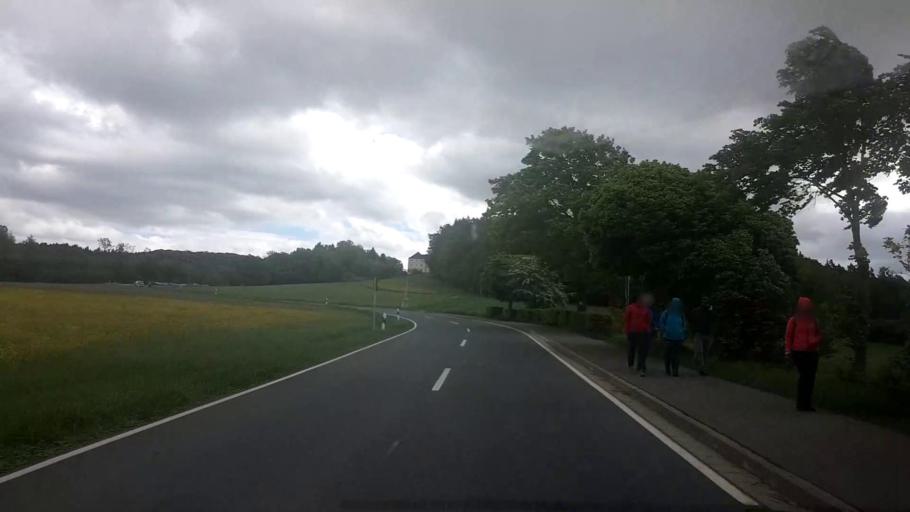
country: DE
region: Bavaria
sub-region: Upper Franconia
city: Lichtenfels
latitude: 50.1193
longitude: 11.0440
